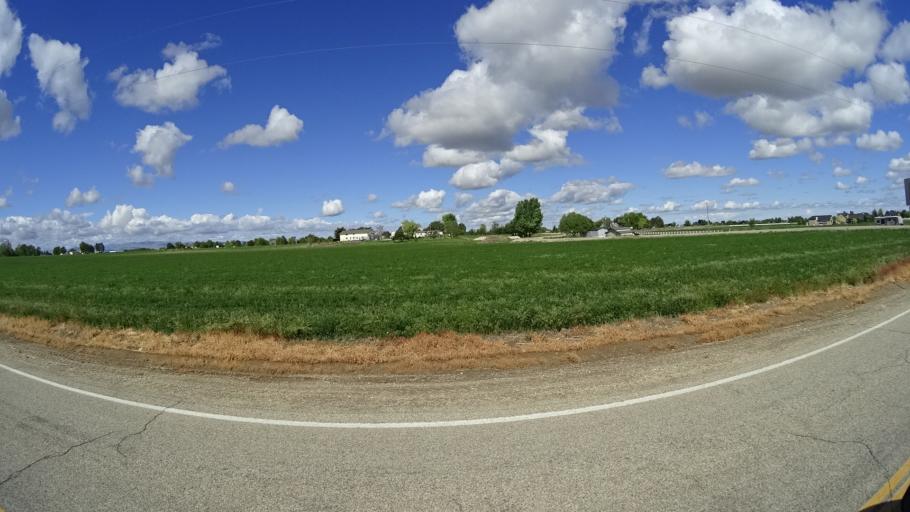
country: US
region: Idaho
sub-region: Ada County
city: Kuna
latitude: 43.5162
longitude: -116.4731
